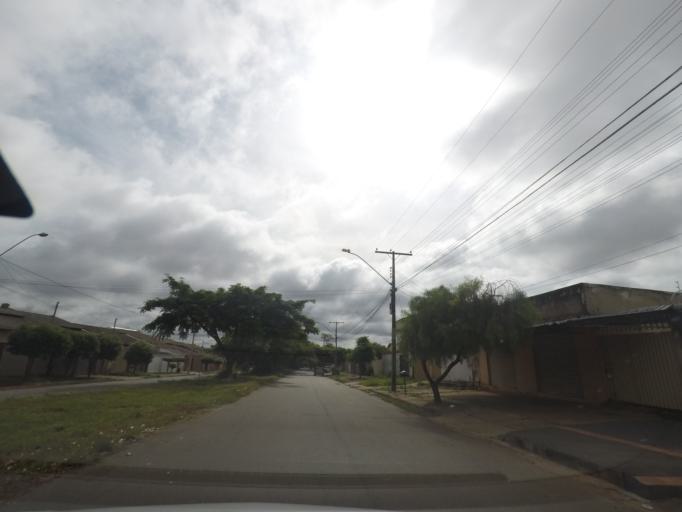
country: BR
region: Goias
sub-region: Goiania
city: Goiania
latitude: -16.7433
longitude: -49.3269
